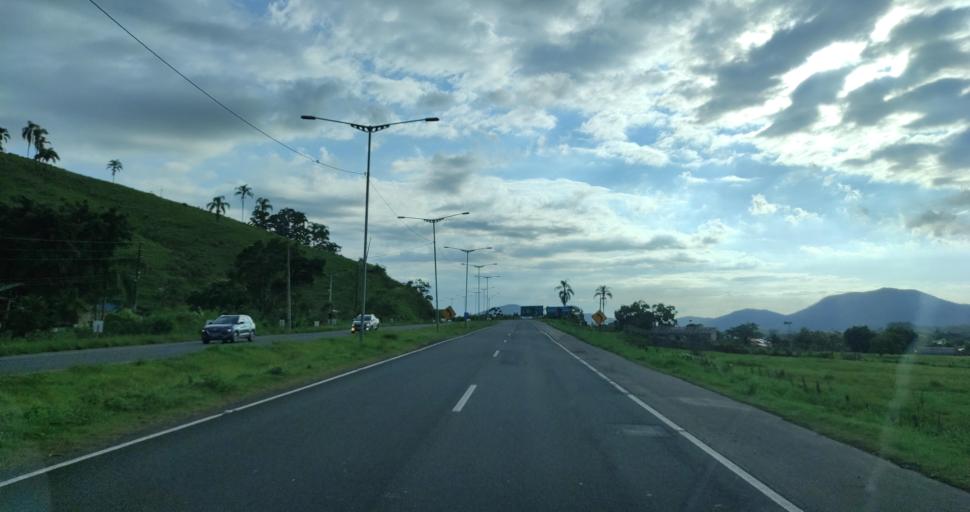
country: BR
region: Santa Catarina
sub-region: Penha
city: Penha
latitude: -26.8088
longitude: -48.6527
